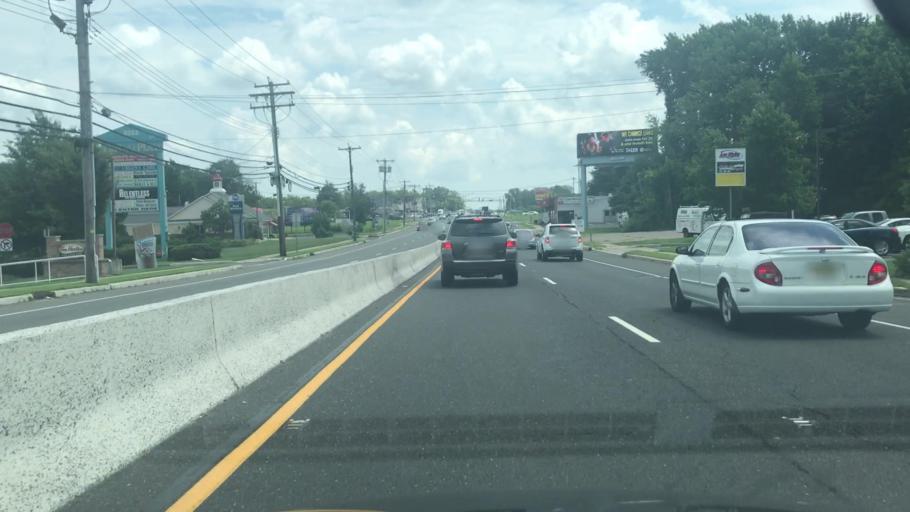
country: US
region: New Jersey
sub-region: Monmouth County
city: Keyport
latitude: 40.4218
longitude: -74.1880
